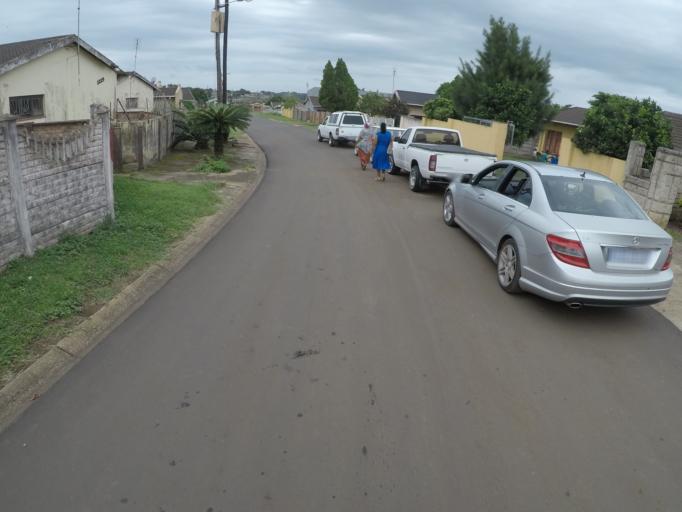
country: ZA
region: KwaZulu-Natal
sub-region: uThungulu District Municipality
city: Empangeni
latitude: -28.7741
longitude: 31.8499
